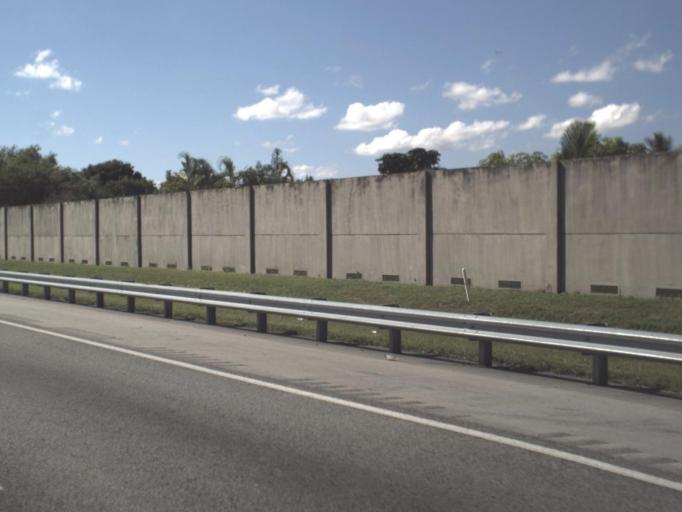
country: US
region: Florida
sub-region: Miami-Dade County
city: University Park
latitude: 25.7436
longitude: -80.3848
